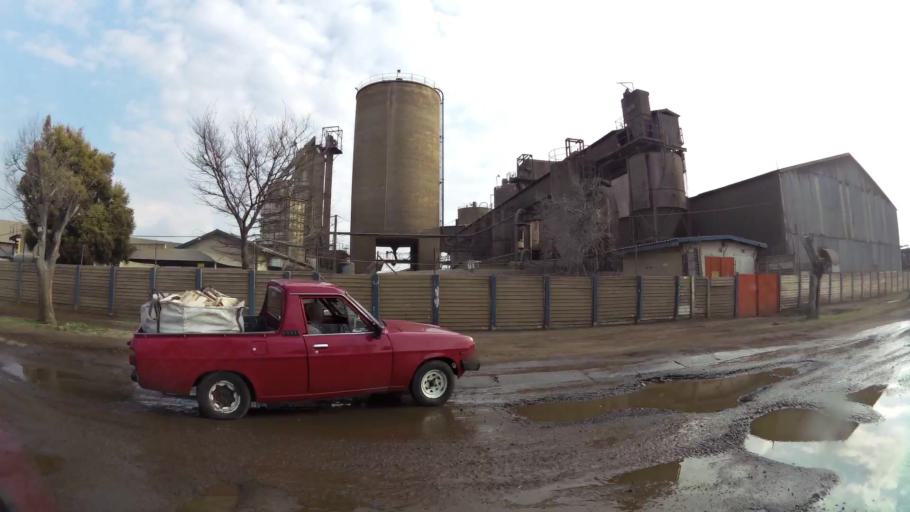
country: ZA
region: Gauteng
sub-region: Sedibeng District Municipality
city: Vereeniging
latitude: -26.6817
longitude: 27.9106
